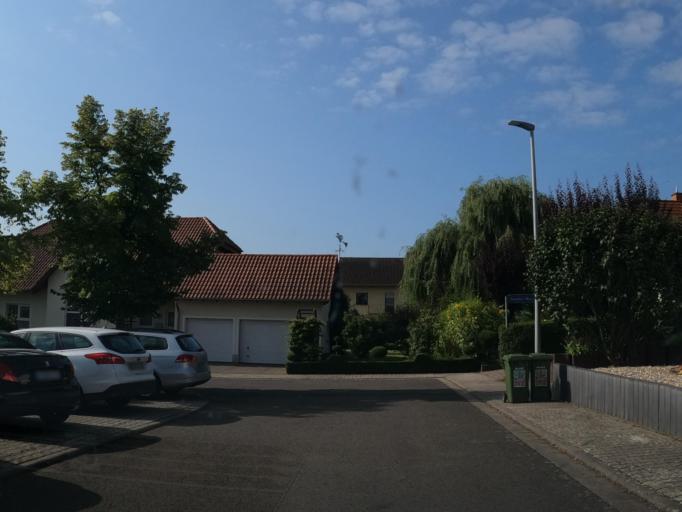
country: DE
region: Rheinland-Pfalz
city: Armsheim
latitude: 49.8127
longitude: 8.0621
